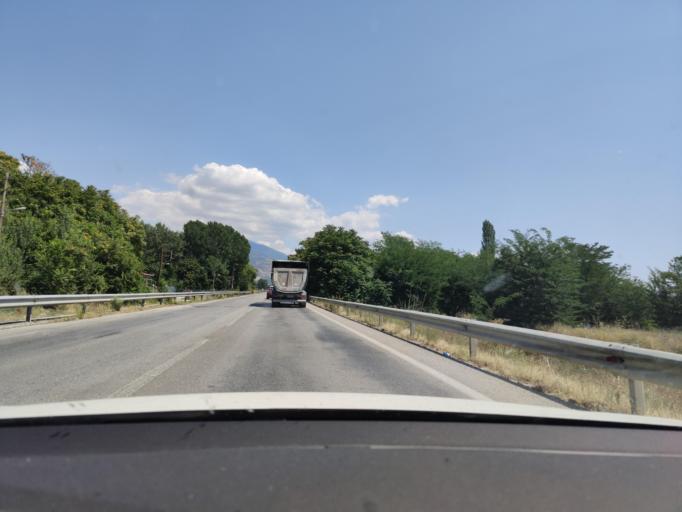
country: GR
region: Central Macedonia
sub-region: Nomos Serron
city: Serres
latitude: 41.0736
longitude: 23.5609
